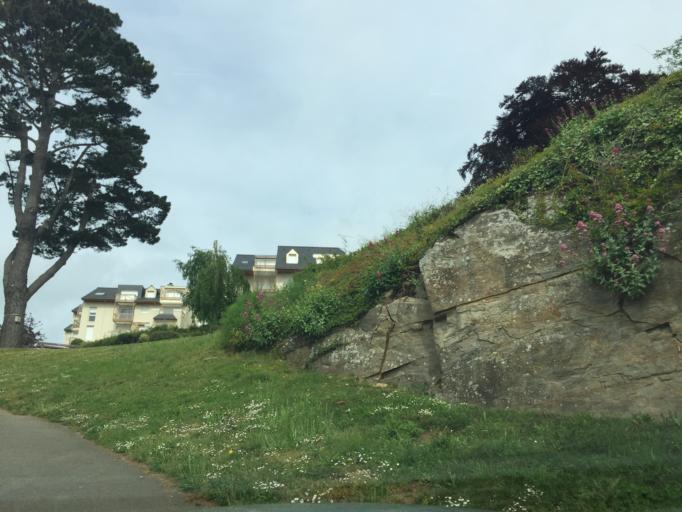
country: FR
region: Brittany
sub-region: Departement des Cotes-d'Armor
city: Saint-Cast-le-Guildo
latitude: 48.6364
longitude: -2.2566
